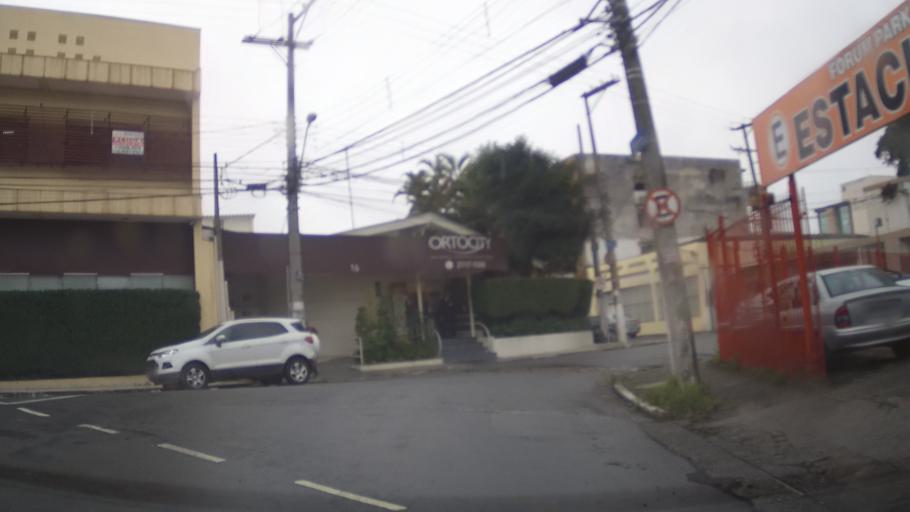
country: BR
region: Sao Paulo
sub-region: Guarulhos
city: Guarulhos
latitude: -23.4683
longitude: -46.5319
